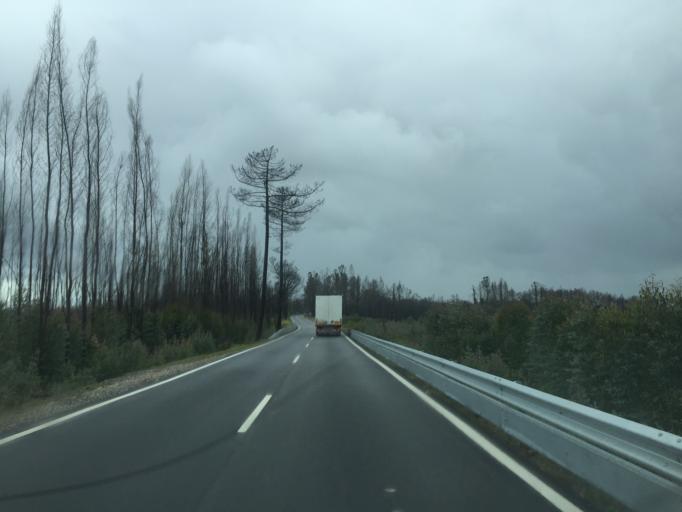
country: PT
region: Coimbra
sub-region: Oliveira do Hospital
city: Oliveira do Hospital
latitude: 40.3267
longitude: -7.9353
